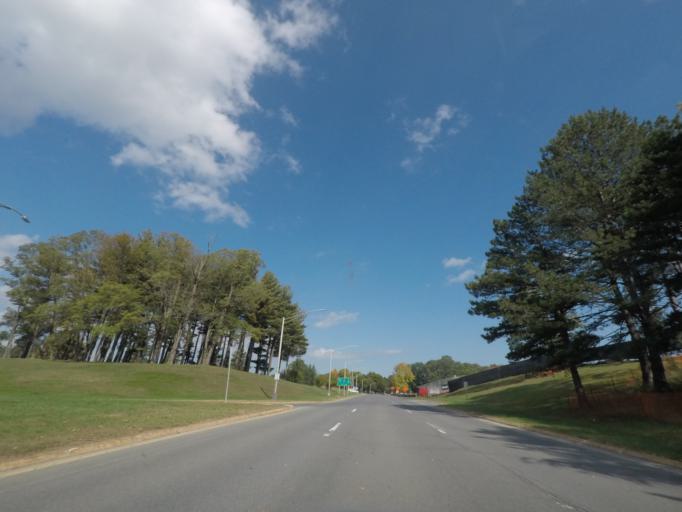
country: US
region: New York
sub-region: Albany County
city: Roessleville
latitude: 42.6818
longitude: -73.8161
